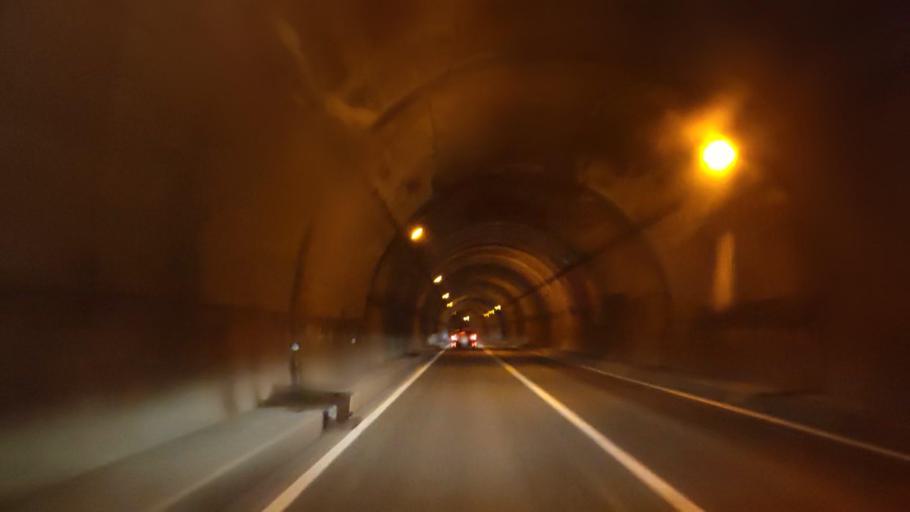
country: JP
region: Niigata
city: Itoigawa
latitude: 36.9502
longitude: 137.8579
